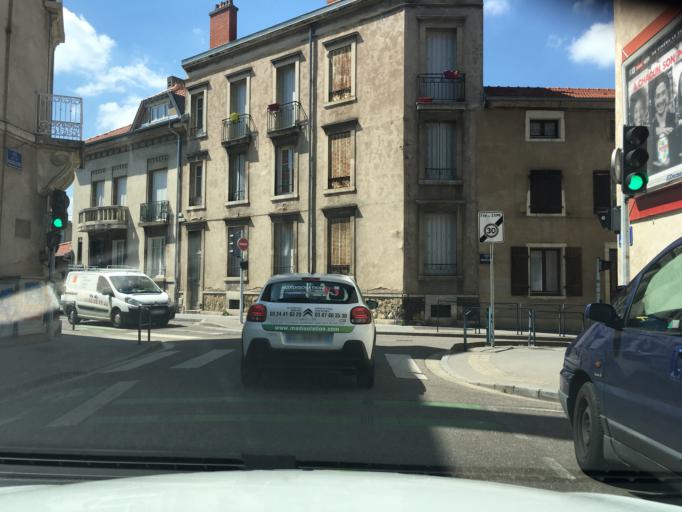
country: FR
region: Lorraine
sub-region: Departement de Meurthe-et-Moselle
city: Nancy
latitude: 48.6791
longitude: 6.1937
